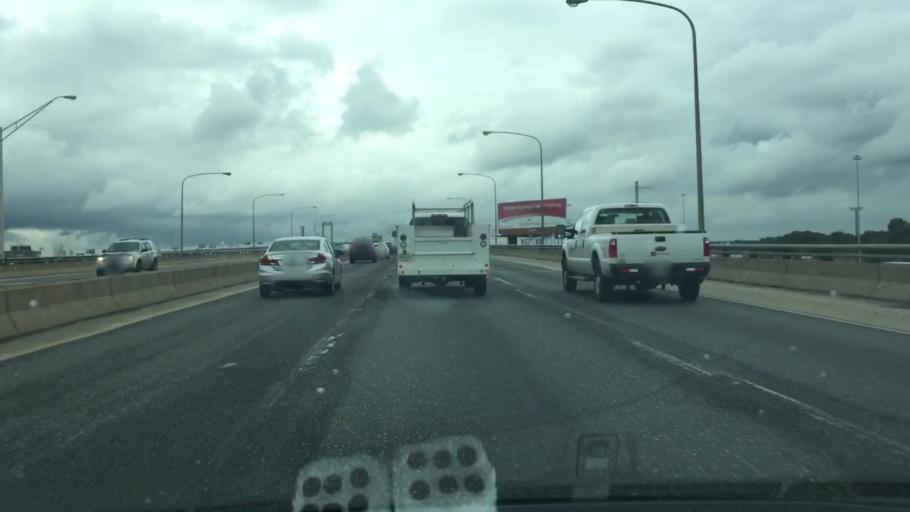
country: US
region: New Jersey
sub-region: Gloucester County
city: National Park
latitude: 39.8988
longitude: -75.1663
